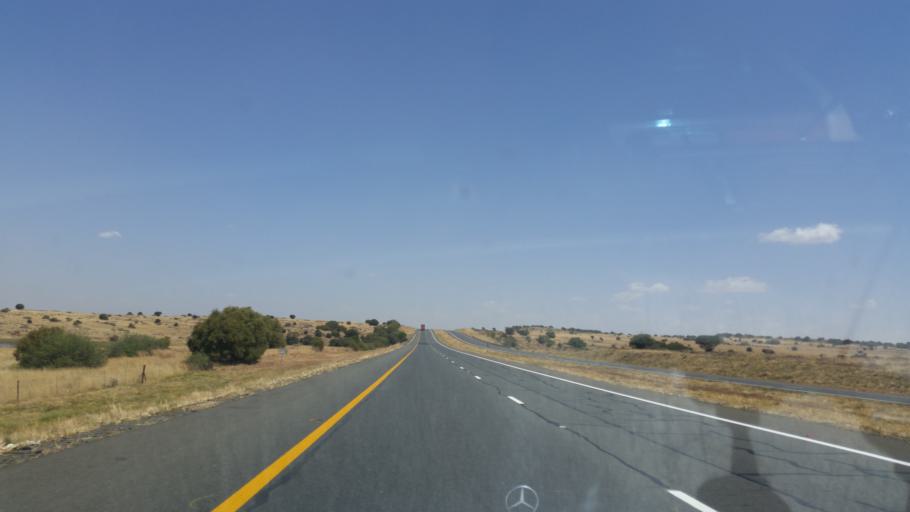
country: ZA
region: Orange Free State
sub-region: Lejweleputswa District Municipality
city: Brandfort
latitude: -28.9127
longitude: 26.4533
